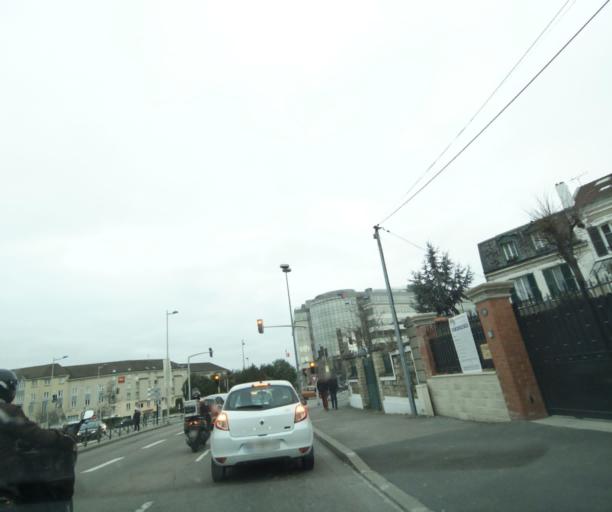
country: FR
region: Ile-de-France
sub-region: Departement des Yvelines
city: Poissy
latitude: 48.9326
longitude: 2.0440
